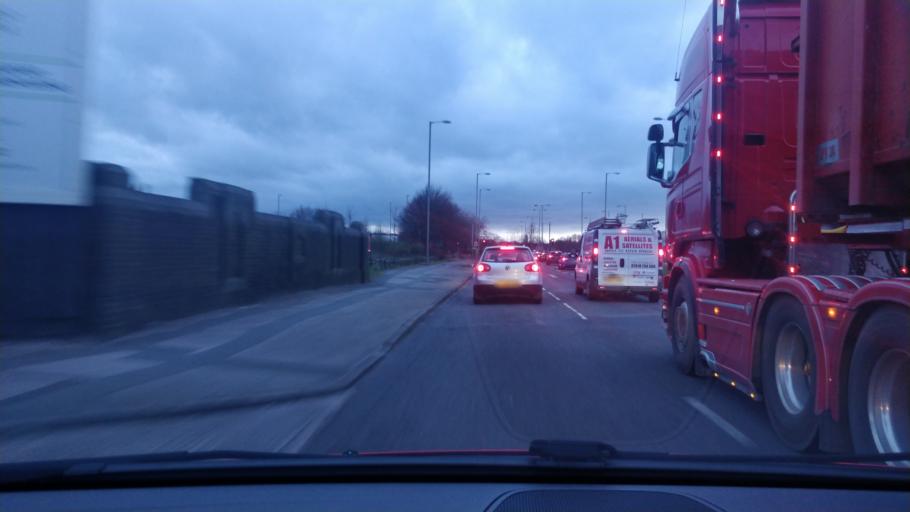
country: GB
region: England
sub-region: Sefton
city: Melling
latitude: 53.4590
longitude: -2.9084
